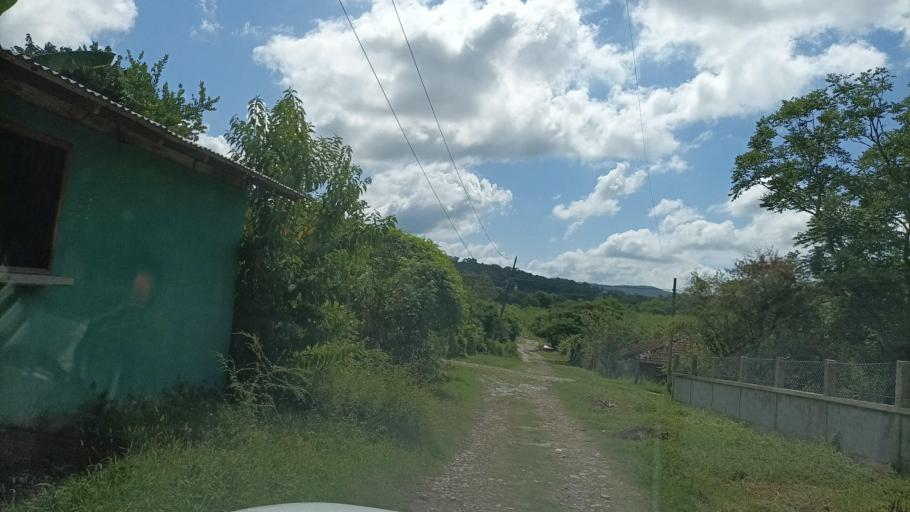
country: MX
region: Veracruz
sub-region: Tantoyuca
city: El Lindero
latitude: 21.1922
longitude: -98.1449
